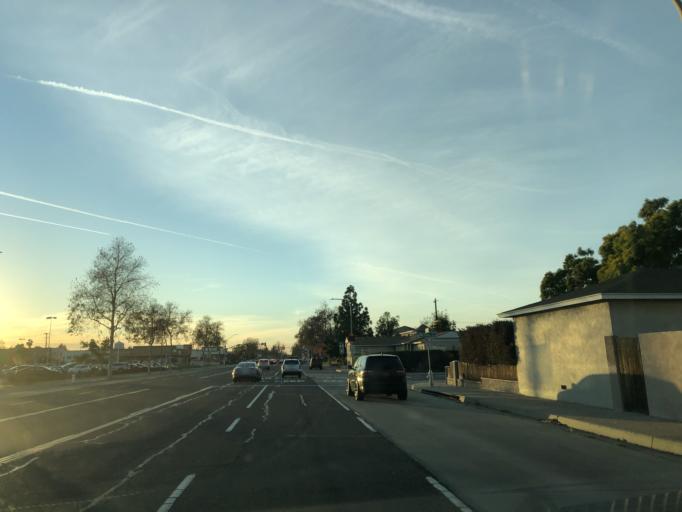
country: US
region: California
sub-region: Orange County
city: Santa Ana
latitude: 33.7600
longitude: -117.8495
